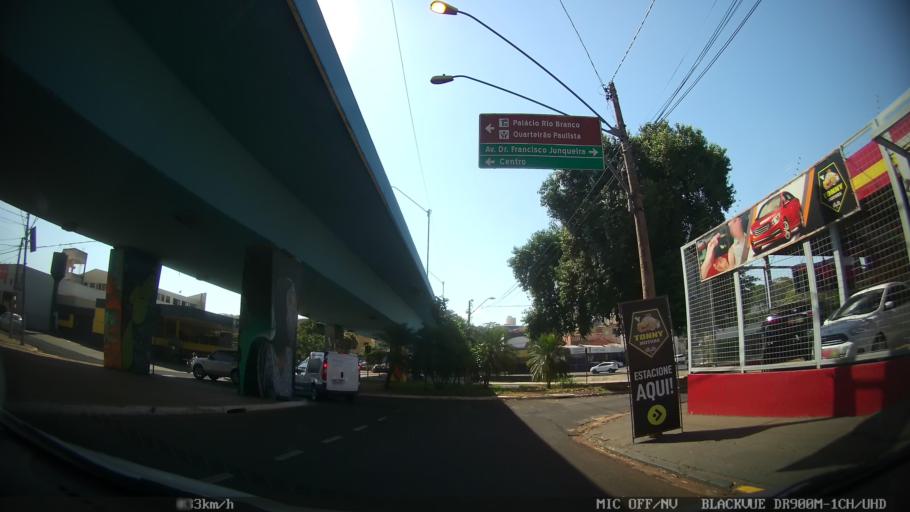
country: BR
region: Sao Paulo
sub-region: Ribeirao Preto
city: Ribeirao Preto
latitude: -21.1809
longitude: -47.8009
